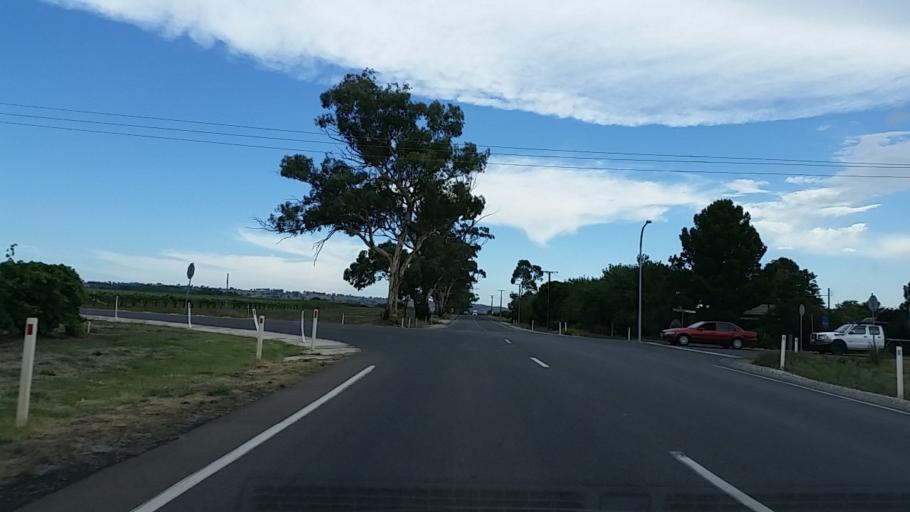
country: AU
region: South Australia
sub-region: Barossa
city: Angaston
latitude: -34.4786
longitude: 139.0337
